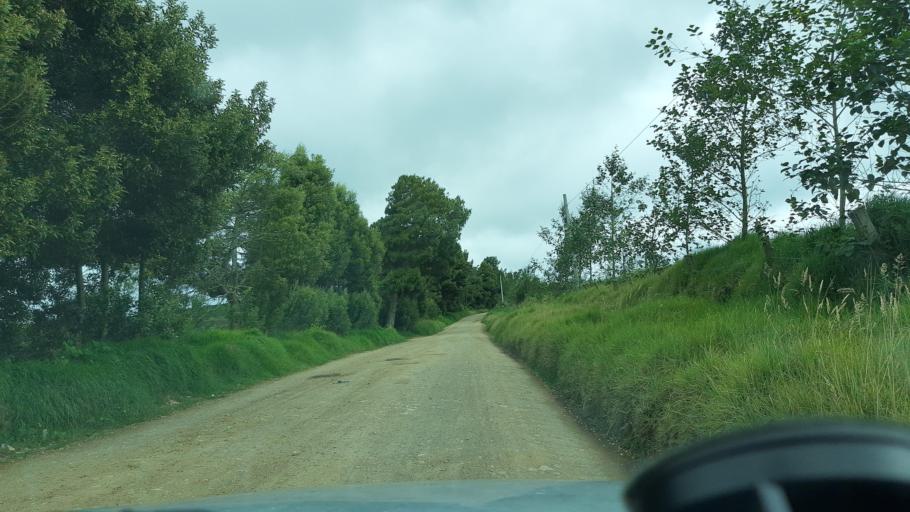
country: CO
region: Boyaca
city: Samaca
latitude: 5.4935
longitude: -73.4546
